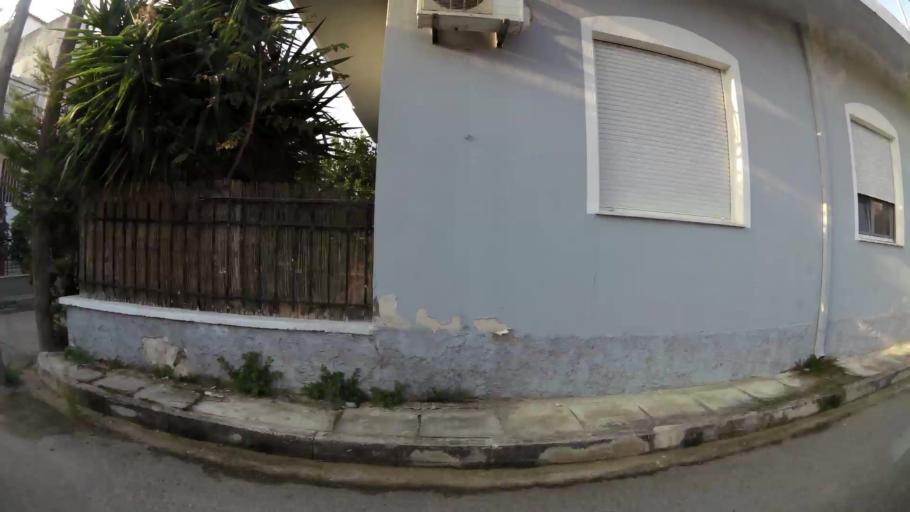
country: GR
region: Attica
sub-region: Nomarchia Dytikis Attikis
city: Zefyri
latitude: 38.0519
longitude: 23.7239
